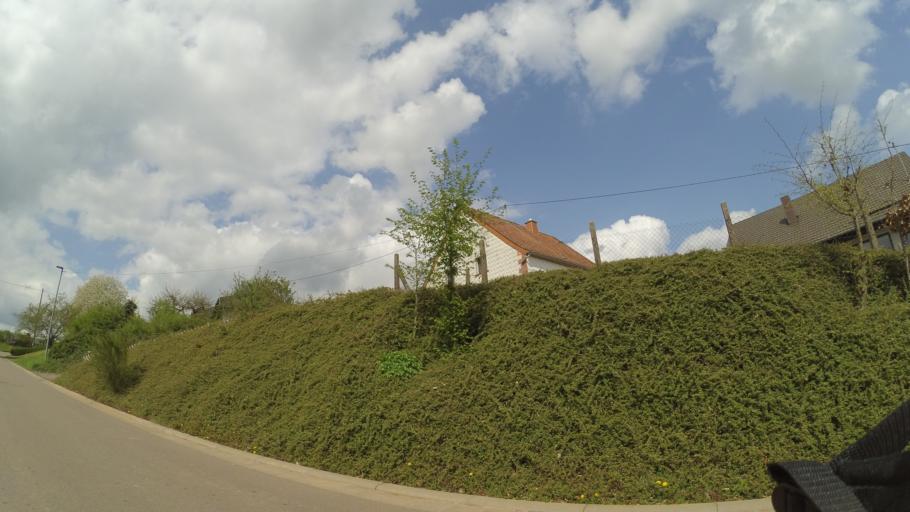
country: DE
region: Saarland
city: Nonnweiler
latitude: 49.5779
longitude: 6.9265
